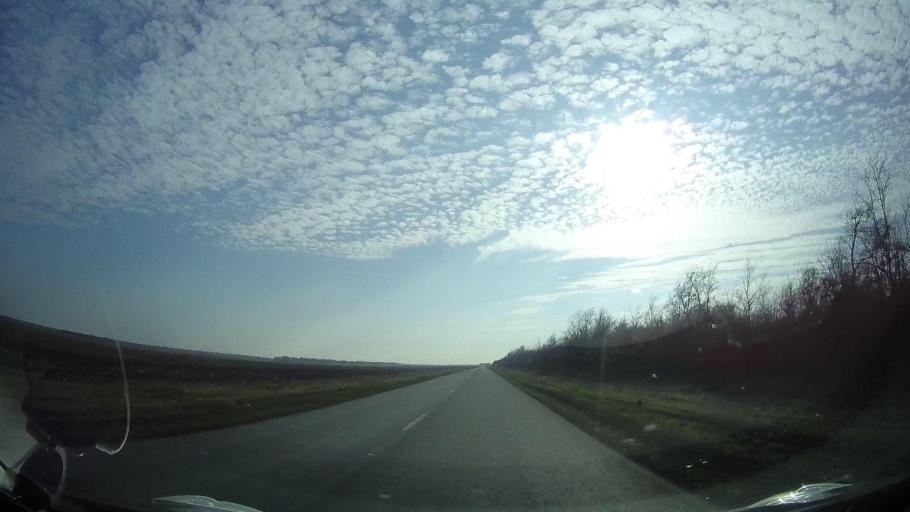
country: RU
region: Rostov
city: Veselyy
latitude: 46.9799
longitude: 40.7197
